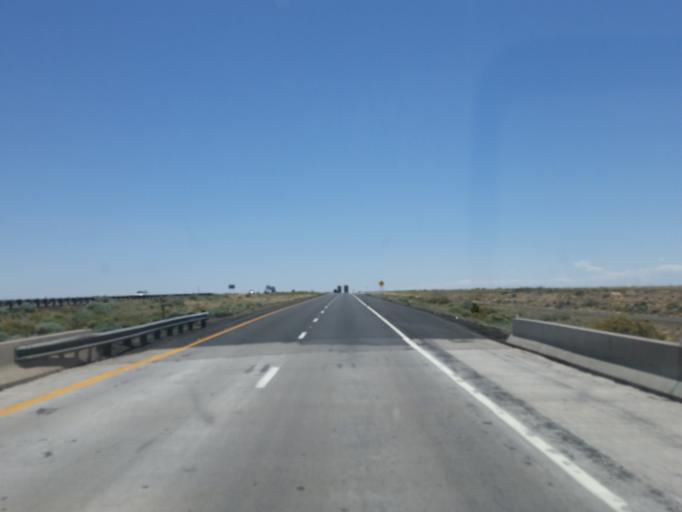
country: US
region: Arizona
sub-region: Coconino County
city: LeChee
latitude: 35.1289
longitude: -111.1839
